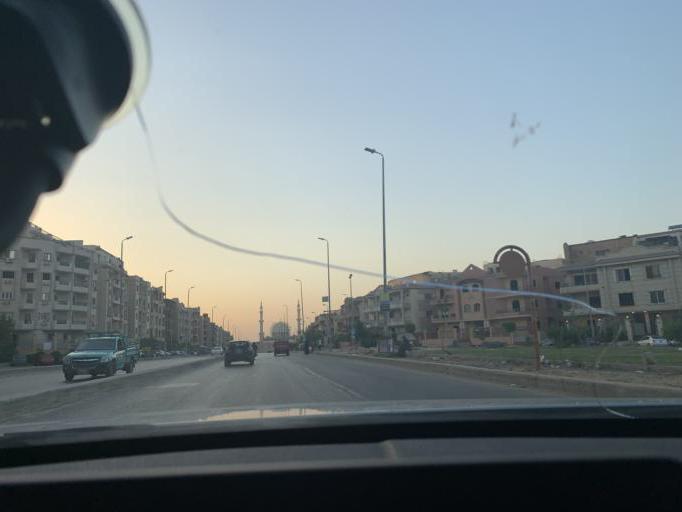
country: EG
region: Muhafazat al Qahirah
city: Cairo
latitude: 30.0017
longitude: 31.4612
